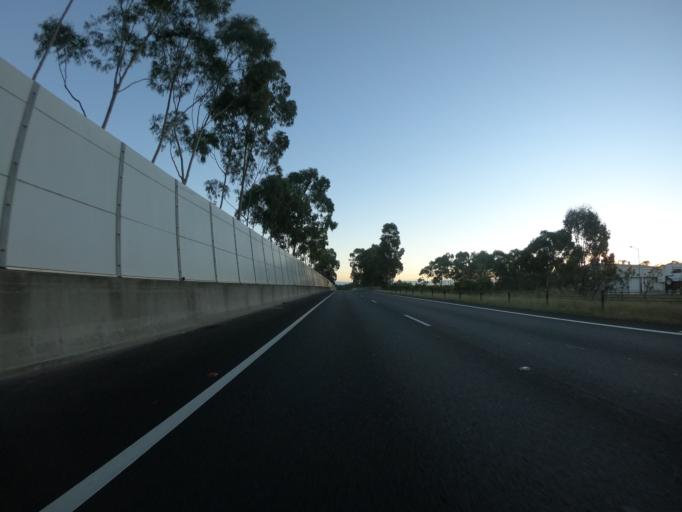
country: AU
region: New South Wales
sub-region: Blacktown
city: Glendenning
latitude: -33.7618
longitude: 150.8466
